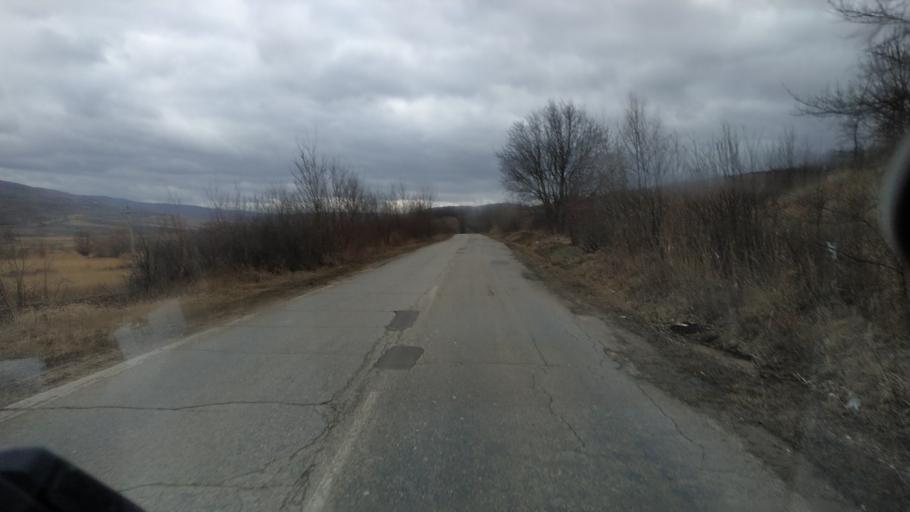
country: MD
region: Calarasi
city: Calarasi
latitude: 47.2385
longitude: 28.1878
